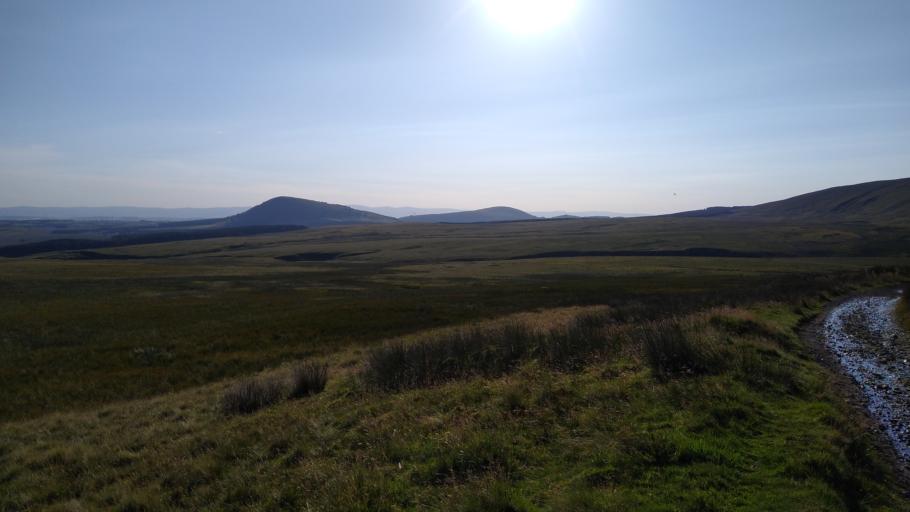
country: GB
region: England
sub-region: Cumbria
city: Keswick
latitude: 54.5996
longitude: -3.0123
